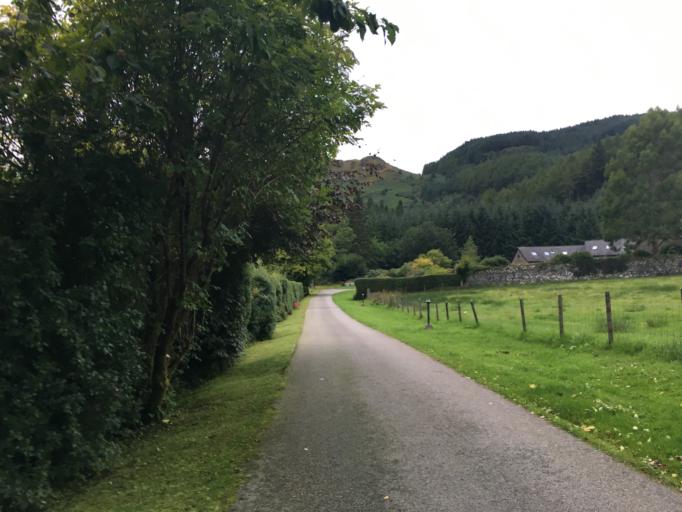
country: GB
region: Scotland
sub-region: Argyll and Bute
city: Oban
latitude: 56.2734
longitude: -5.4944
